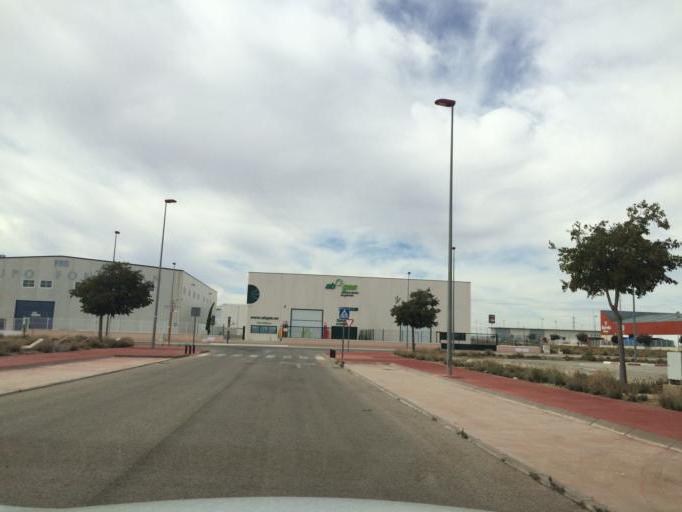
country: ES
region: Castille-La Mancha
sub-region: Provincia de Albacete
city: Albacete
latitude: 39.0282
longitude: -1.8893
